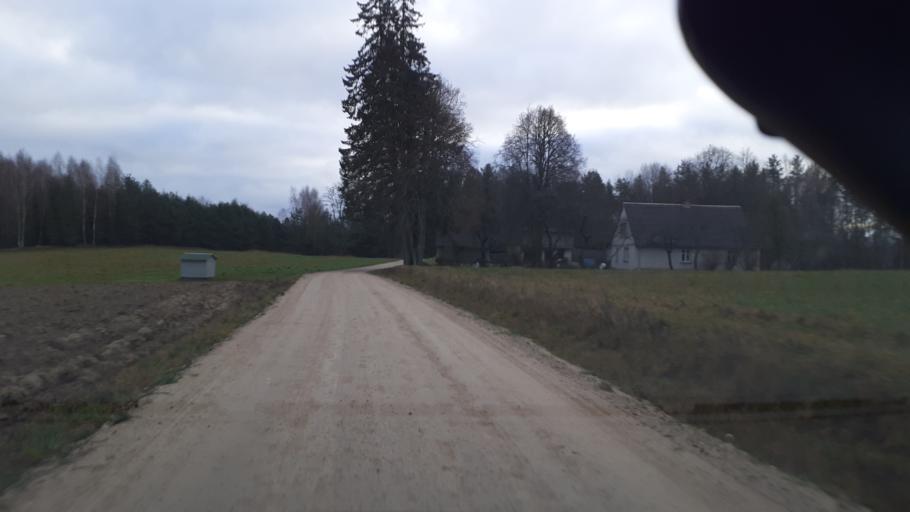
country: LV
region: Kuldigas Rajons
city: Kuldiga
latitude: 56.9053
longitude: 21.9044
